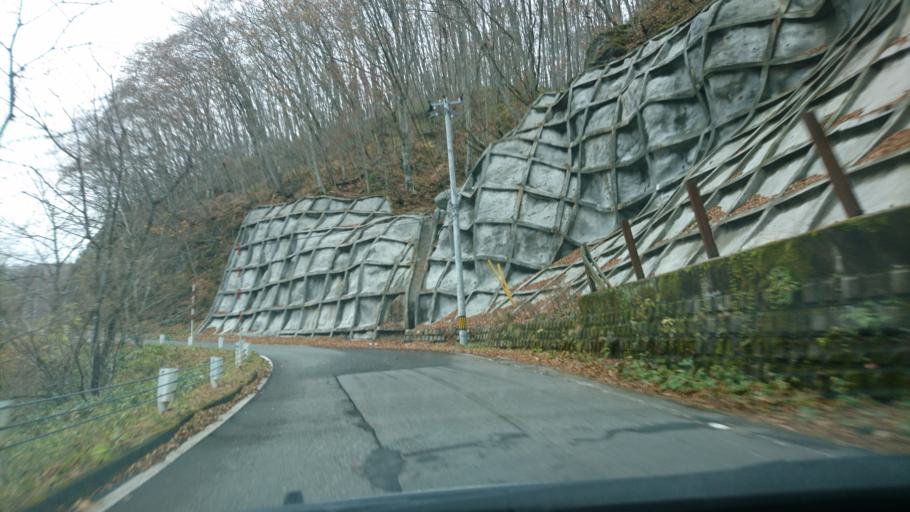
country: JP
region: Iwate
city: Ichinoseki
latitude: 38.9134
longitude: 140.8503
